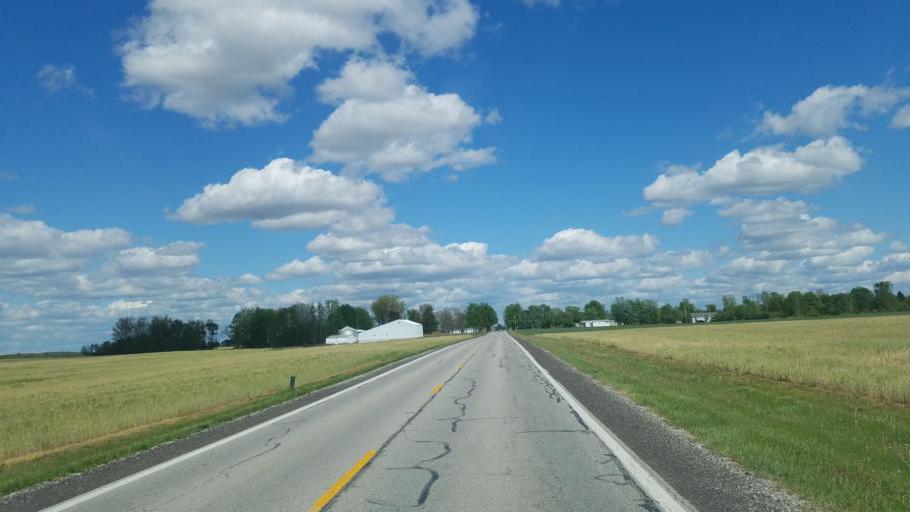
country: US
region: Ohio
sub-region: Marion County
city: Prospect
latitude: 40.4517
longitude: -83.1448
